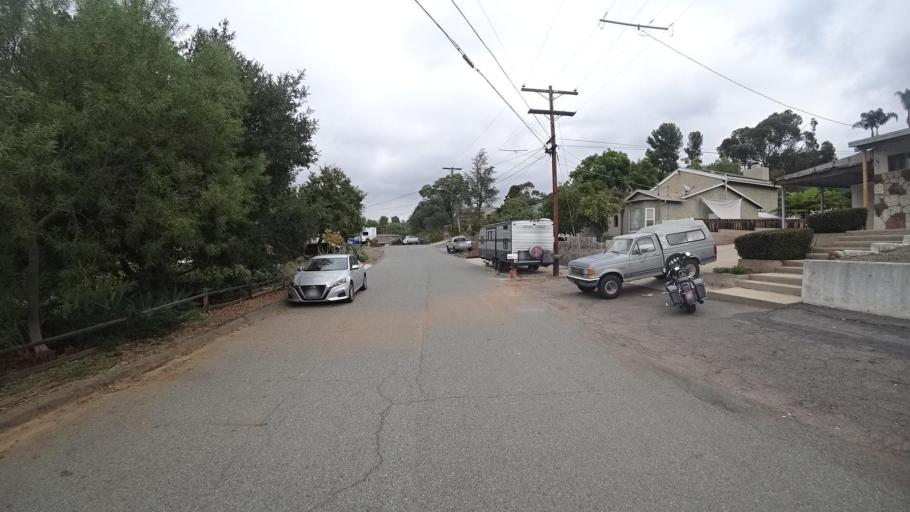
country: US
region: California
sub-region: San Diego County
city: Spring Valley
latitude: 32.7537
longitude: -116.9977
